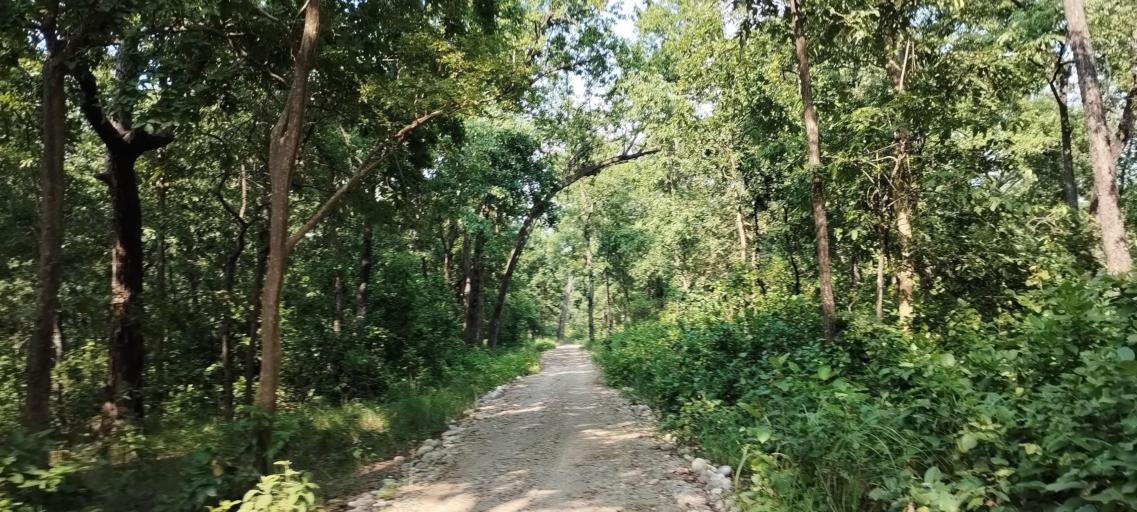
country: NP
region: Far Western
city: Tikapur
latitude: 28.5633
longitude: 81.2664
